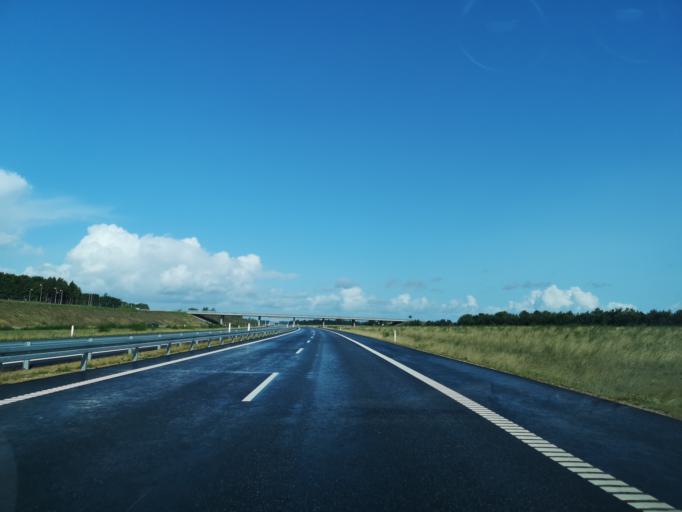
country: DK
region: Central Jutland
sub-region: Herning Kommune
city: Snejbjerg
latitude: 56.1951
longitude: 8.8848
